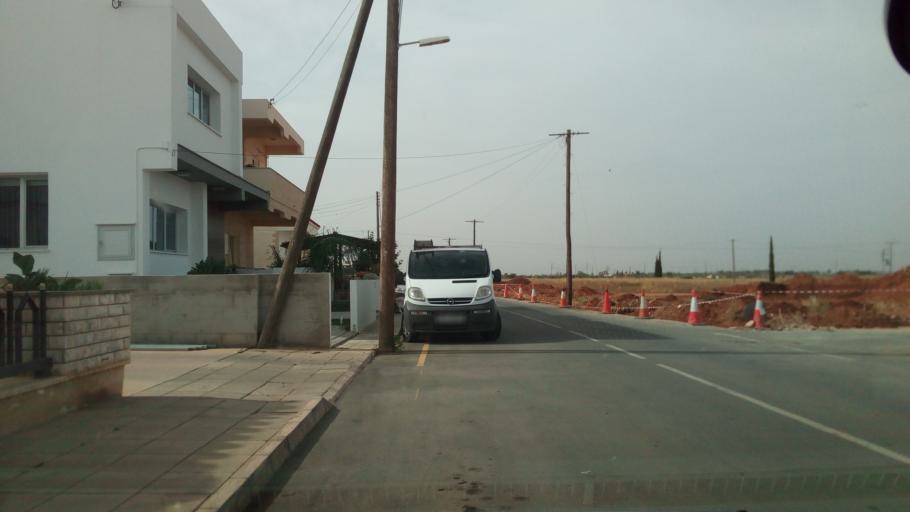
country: CY
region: Larnaka
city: Xylotymbou
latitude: 35.0224
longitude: 33.7429
